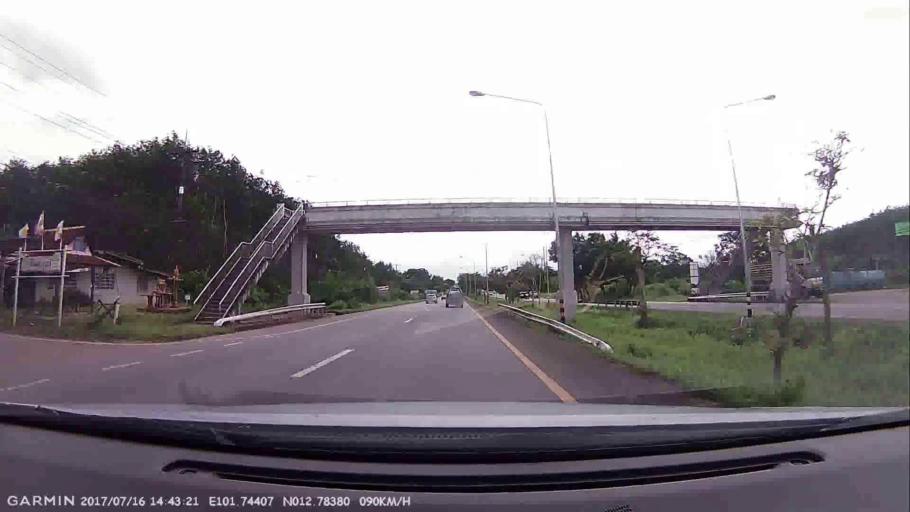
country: TH
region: Chanthaburi
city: Na Yai Am
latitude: 12.7837
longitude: 101.7438
